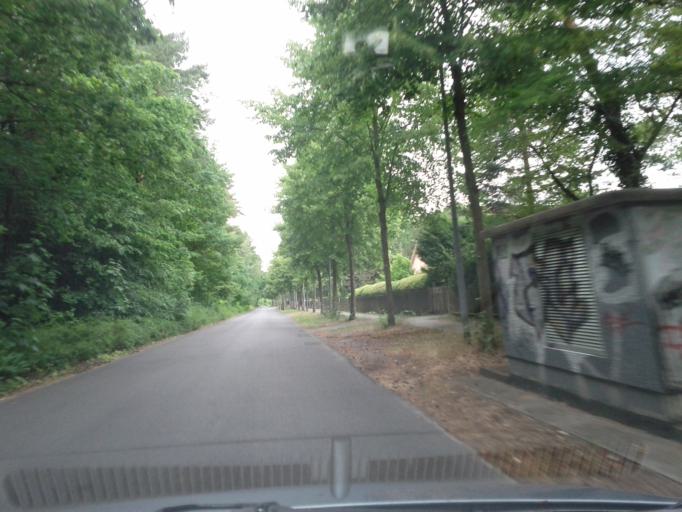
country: DE
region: Brandenburg
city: Schoneiche
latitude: 52.4637
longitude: 13.7107
